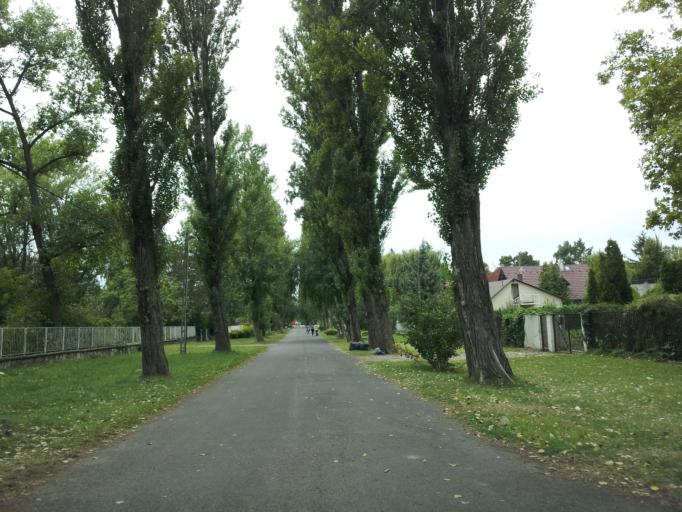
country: HU
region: Somogy
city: Zamardi
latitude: 46.8822
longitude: 17.9335
